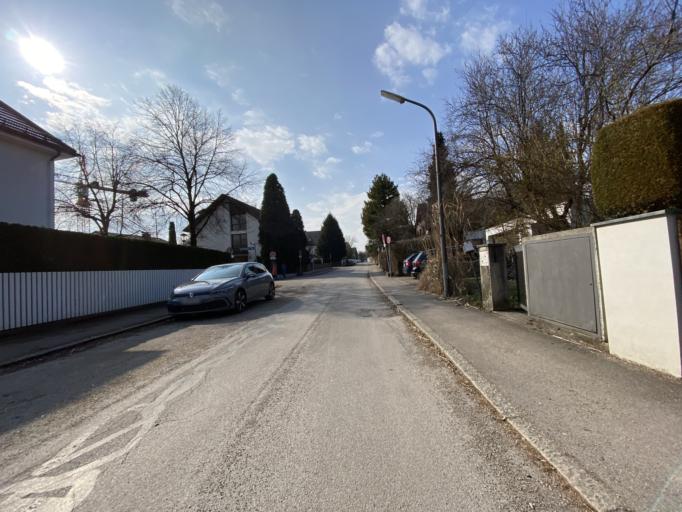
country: DE
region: Bavaria
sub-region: Upper Bavaria
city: Bogenhausen
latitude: 48.1532
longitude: 11.6437
